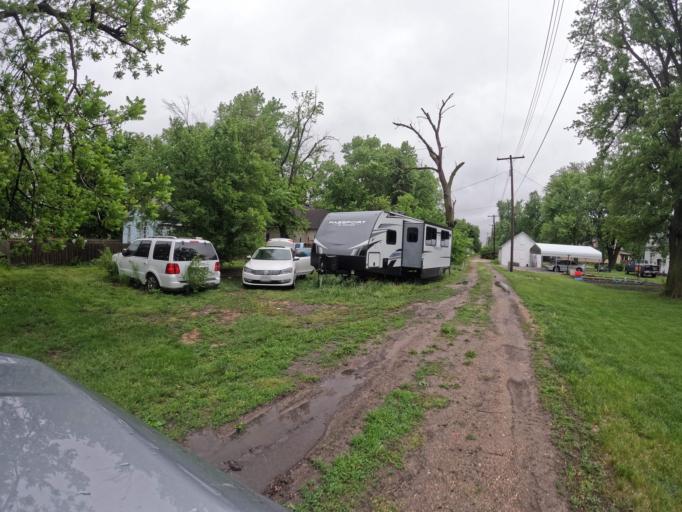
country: US
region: Nebraska
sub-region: Clay County
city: Harvard
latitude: 40.6232
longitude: -98.0979
